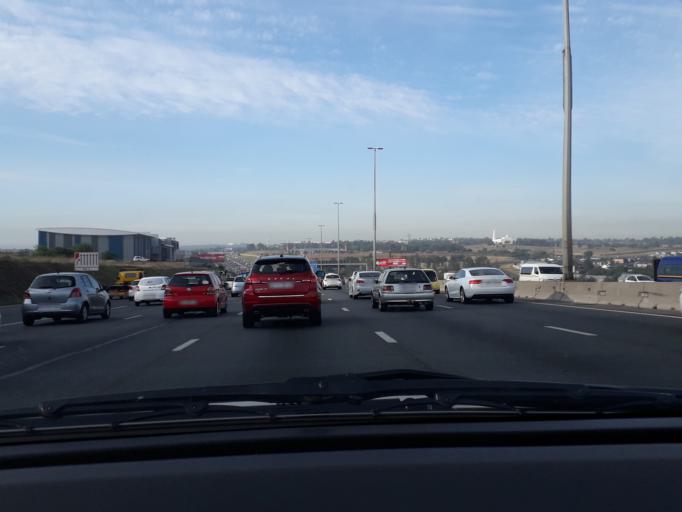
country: ZA
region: Gauteng
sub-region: City of Johannesburg Metropolitan Municipality
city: Midrand
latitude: -26.0236
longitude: 28.1118
